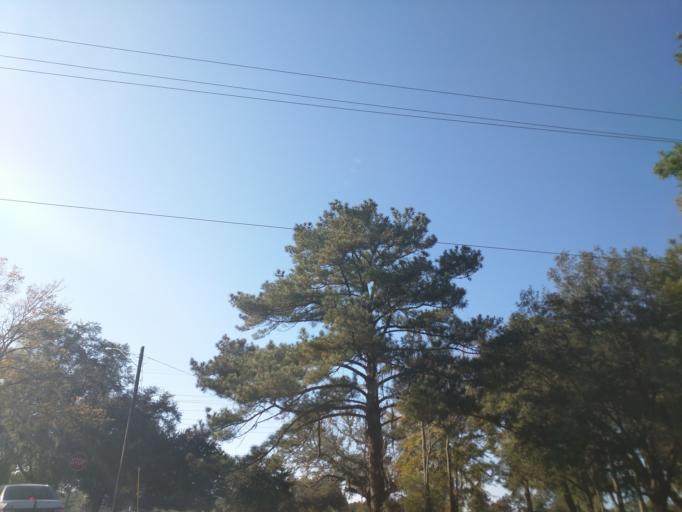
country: US
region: Florida
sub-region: Leon County
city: Tallahassee
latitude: 30.4478
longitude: -84.2151
